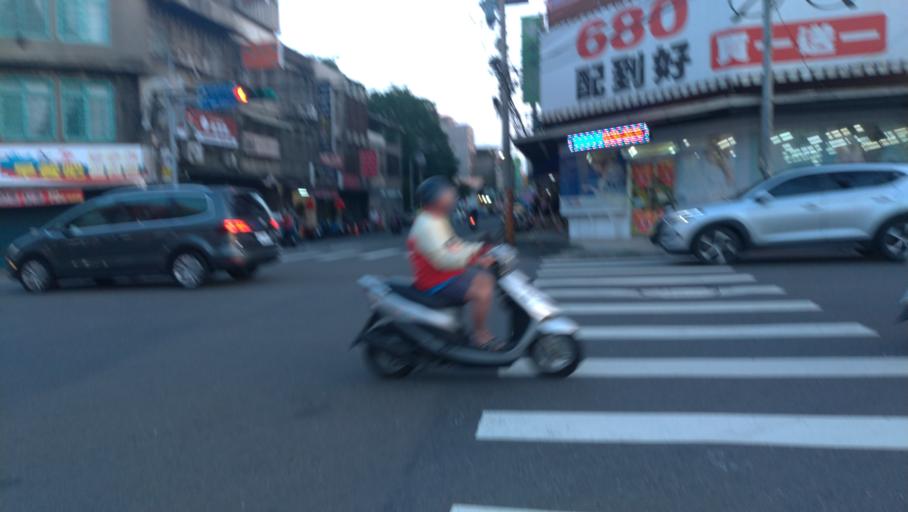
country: TW
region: Taiwan
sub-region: Taoyuan
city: Taoyuan
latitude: 24.9858
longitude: 121.3143
